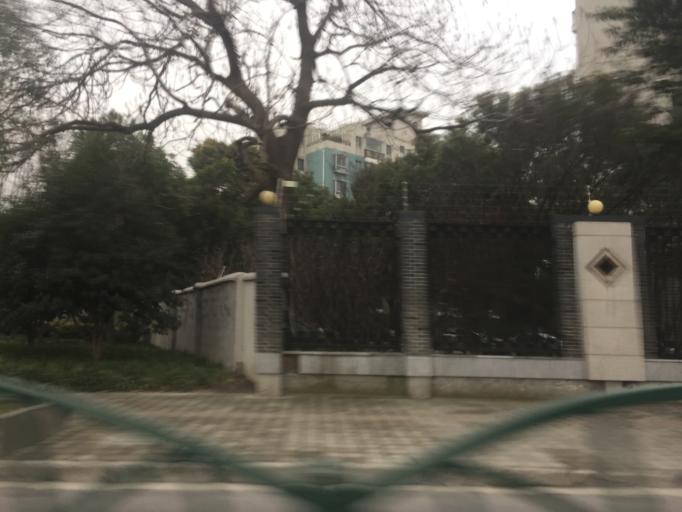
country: CN
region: Shanghai Shi
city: Luwan
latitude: 31.1880
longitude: 121.4965
